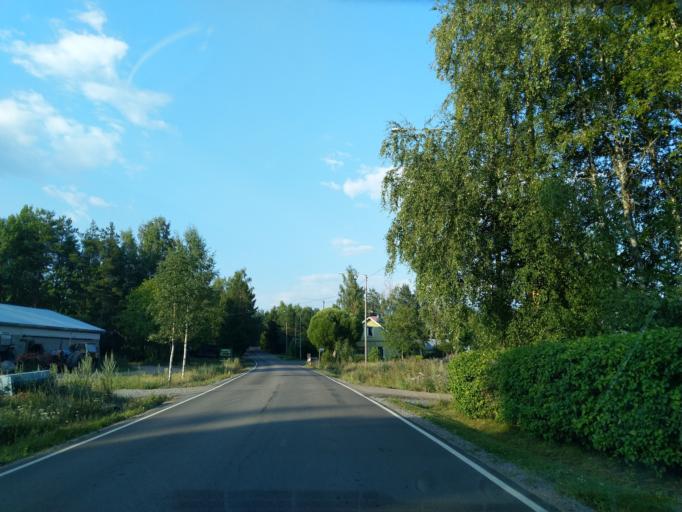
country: FI
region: Satakunta
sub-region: Pohjois-Satakunta
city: Honkajoki
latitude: 61.8211
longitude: 22.2004
